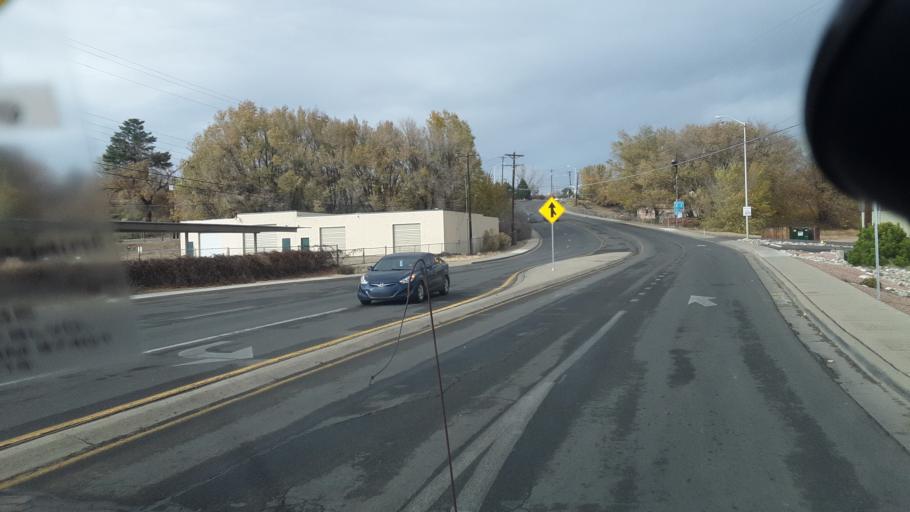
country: US
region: New Mexico
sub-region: San Juan County
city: Farmington
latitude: 36.7310
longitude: -108.1975
